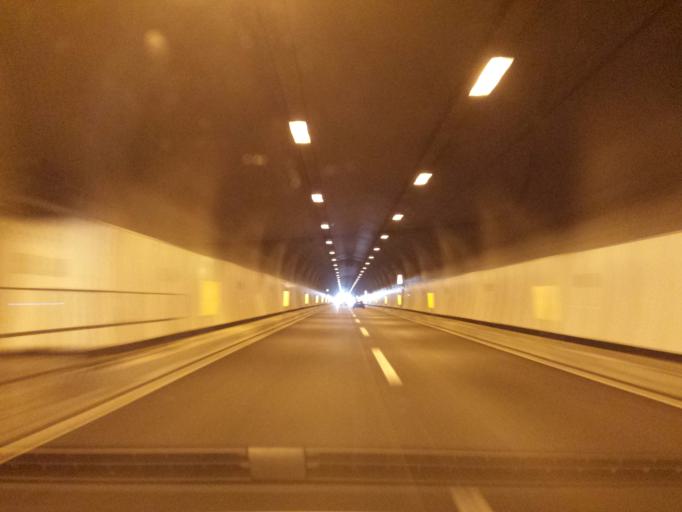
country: IT
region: Veneto
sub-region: Provincia di Vicenza
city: Arcugnano-Torri
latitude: 45.5166
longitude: 11.5424
